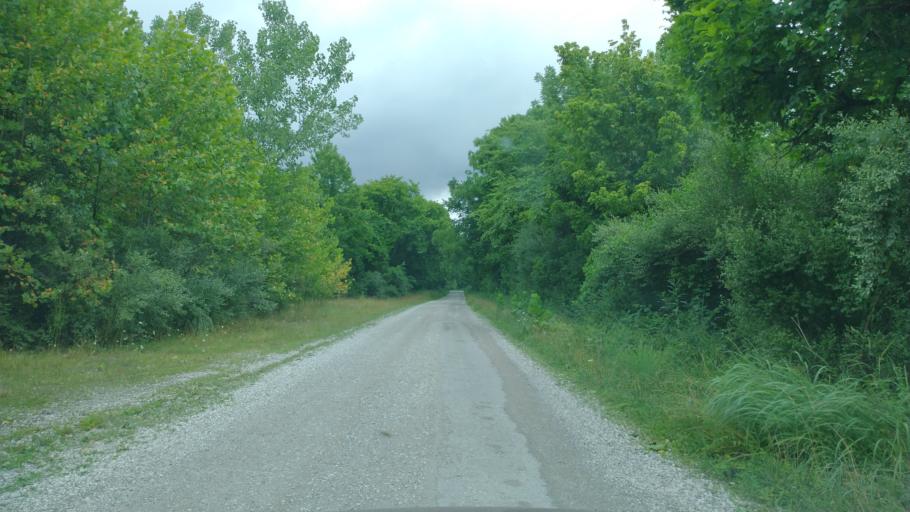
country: US
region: Ohio
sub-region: Meigs County
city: Middleport
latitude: 38.9286
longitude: -82.0696
